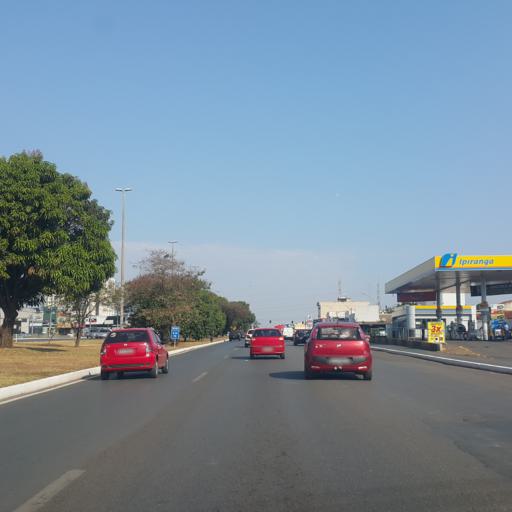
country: BR
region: Federal District
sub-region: Brasilia
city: Brasilia
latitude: -15.8484
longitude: -48.0426
